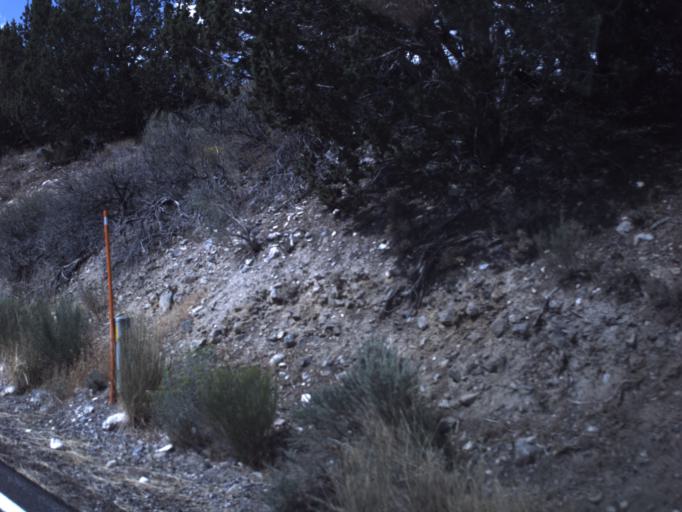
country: US
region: Utah
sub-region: Tooele County
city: Grantsville
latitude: 40.3414
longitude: -112.5382
